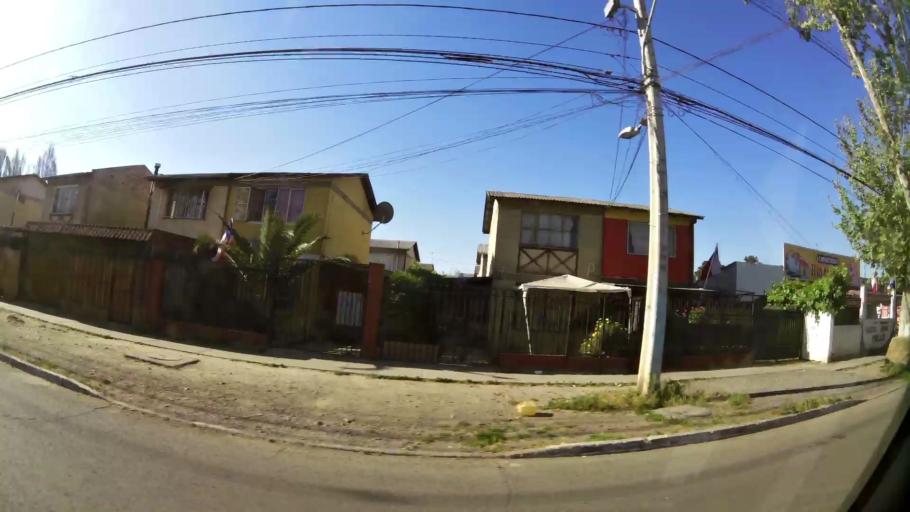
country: CL
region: Santiago Metropolitan
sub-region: Provincia de Talagante
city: Penaflor
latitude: -33.6059
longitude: -70.8638
